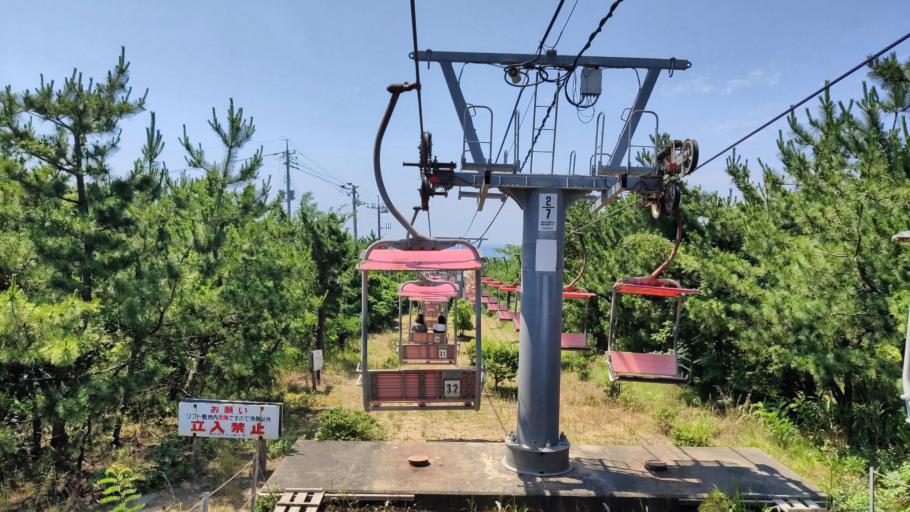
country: JP
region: Tottori
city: Tottori
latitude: 35.5419
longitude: 134.2376
